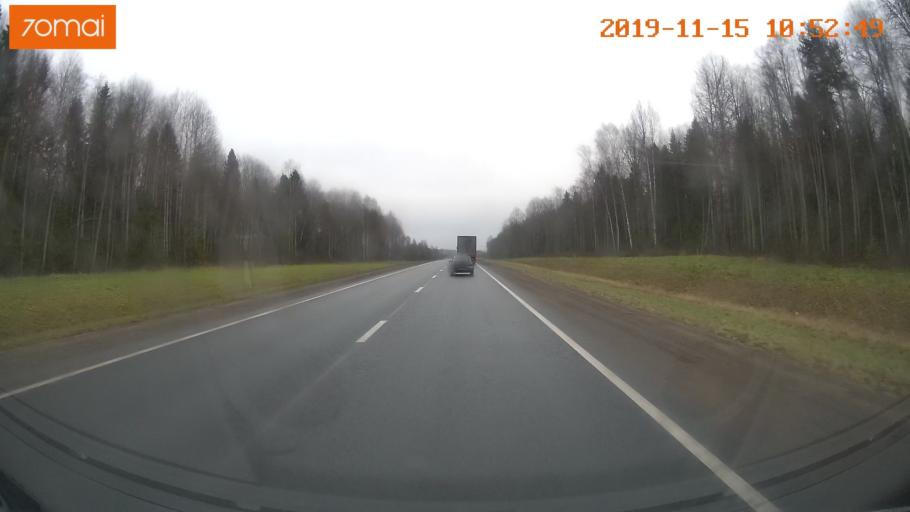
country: RU
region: Vologda
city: Chebsara
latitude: 59.1722
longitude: 38.7407
